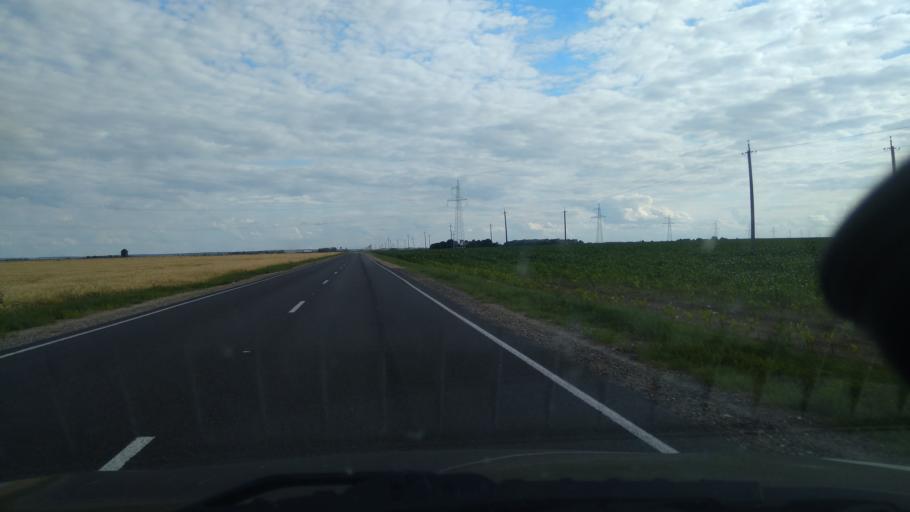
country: BY
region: Grodnenskaya
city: Masty
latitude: 53.3003
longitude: 24.6889
